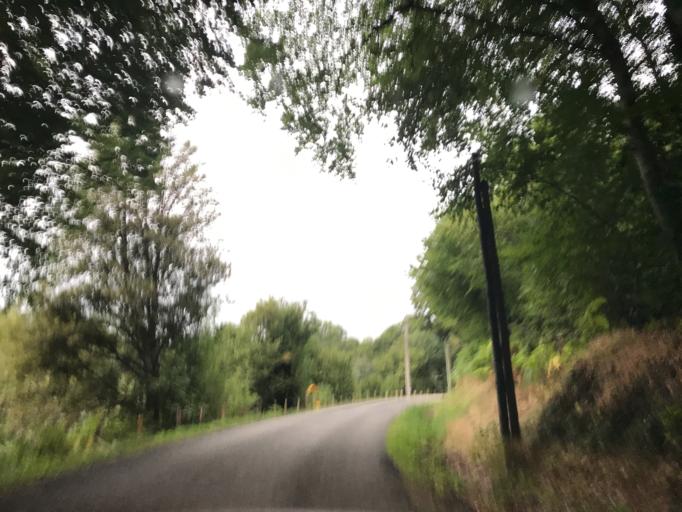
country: FR
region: Auvergne
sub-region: Departement du Puy-de-Dome
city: Thiers
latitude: 45.8436
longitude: 3.5724
